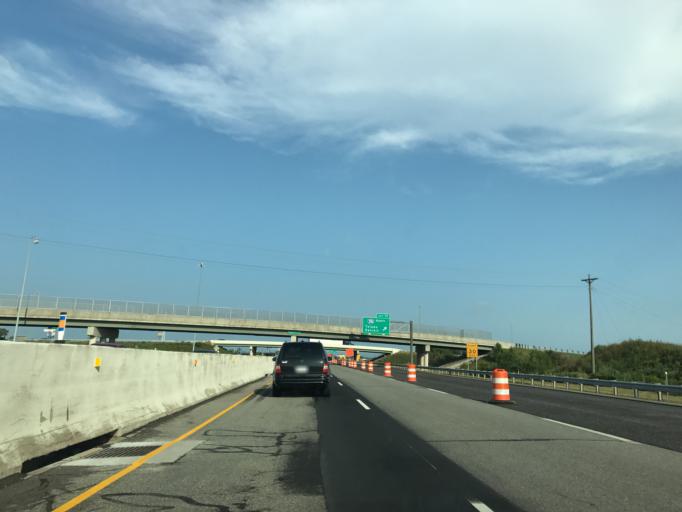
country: US
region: Ohio
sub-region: Wood County
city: Millbury
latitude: 41.5216
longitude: -83.4516
